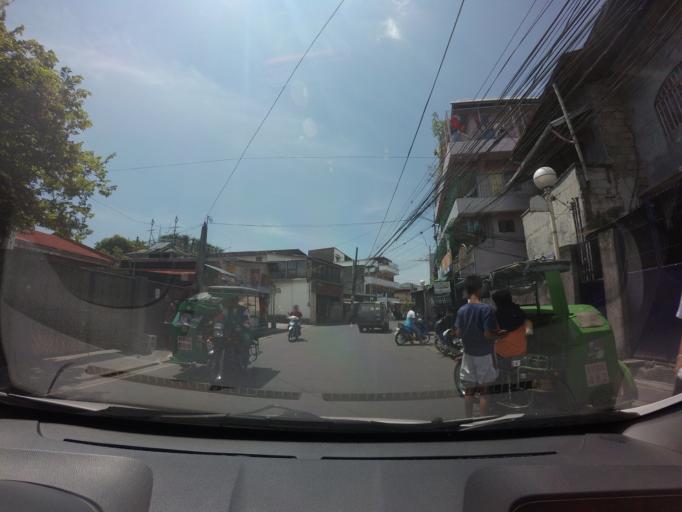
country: PH
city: Sambayanihan People's Village
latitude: 14.4296
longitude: 121.0130
